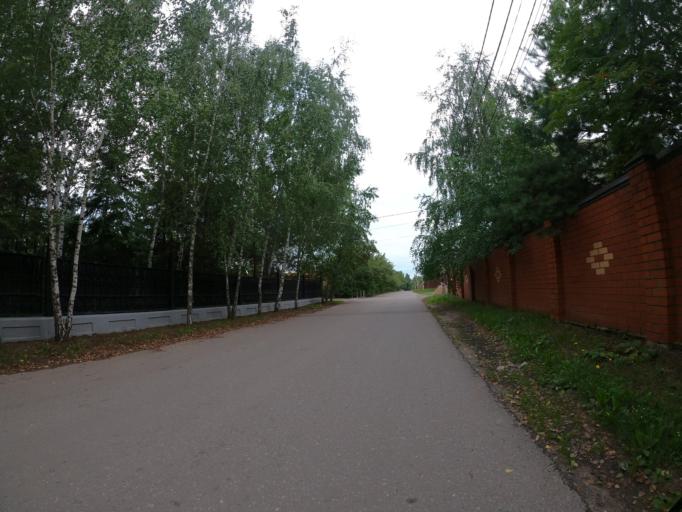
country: RU
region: Moskovskaya
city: Rodniki
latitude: 55.6573
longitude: 38.0717
